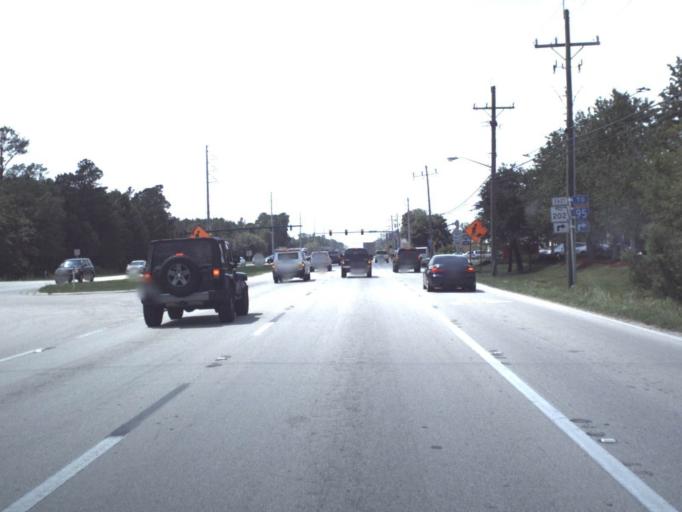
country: US
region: Florida
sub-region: Duval County
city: Jacksonville
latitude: 30.2427
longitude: -81.5989
